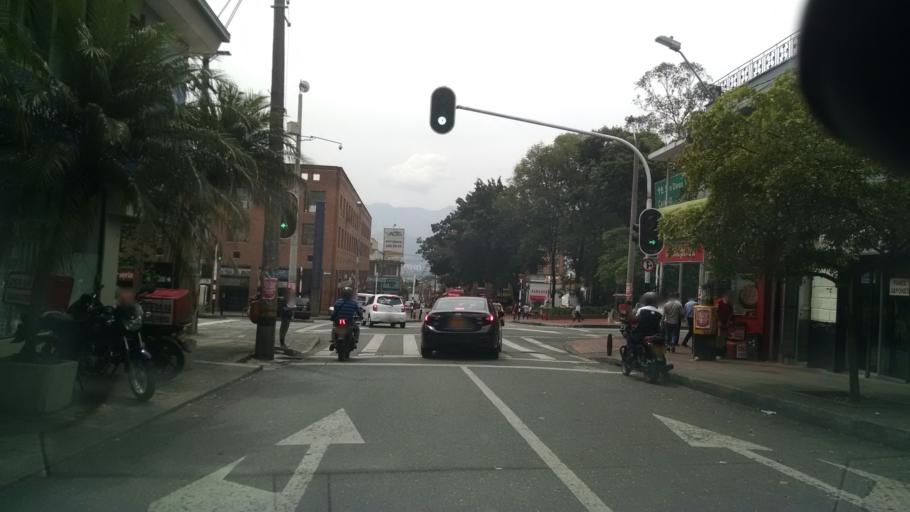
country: CO
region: Antioquia
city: Itagui
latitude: 6.2097
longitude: -75.5704
